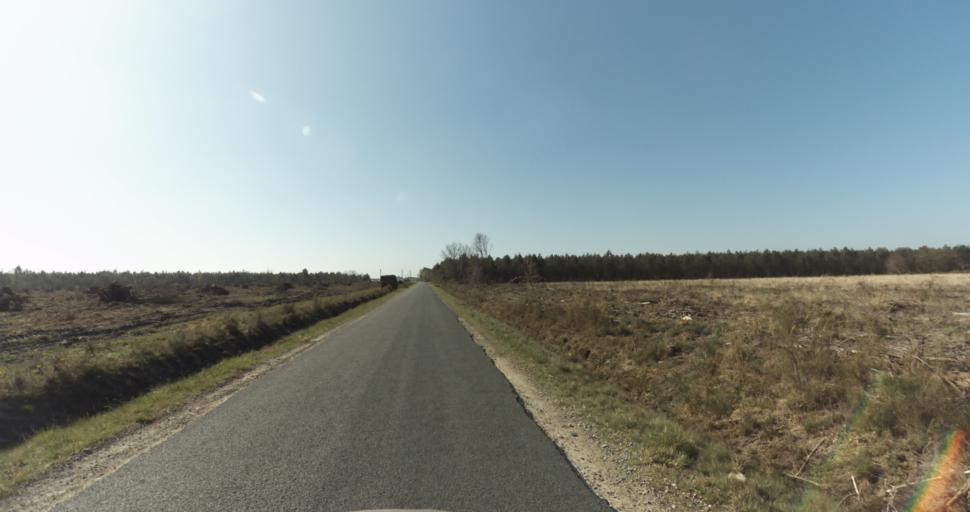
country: FR
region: Aquitaine
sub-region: Departement de la Gironde
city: Marcheprime
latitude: 44.7785
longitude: -0.8598
